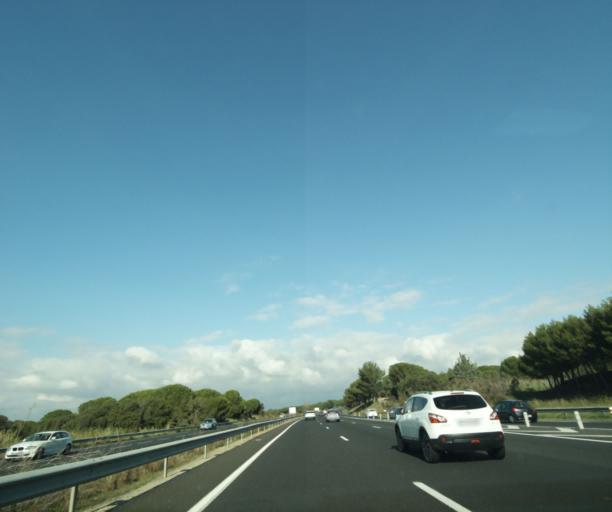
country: FR
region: Languedoc-Roussillon
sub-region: Departement de l'Aude
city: Vinassan
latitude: 43.2180
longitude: 3.0926
